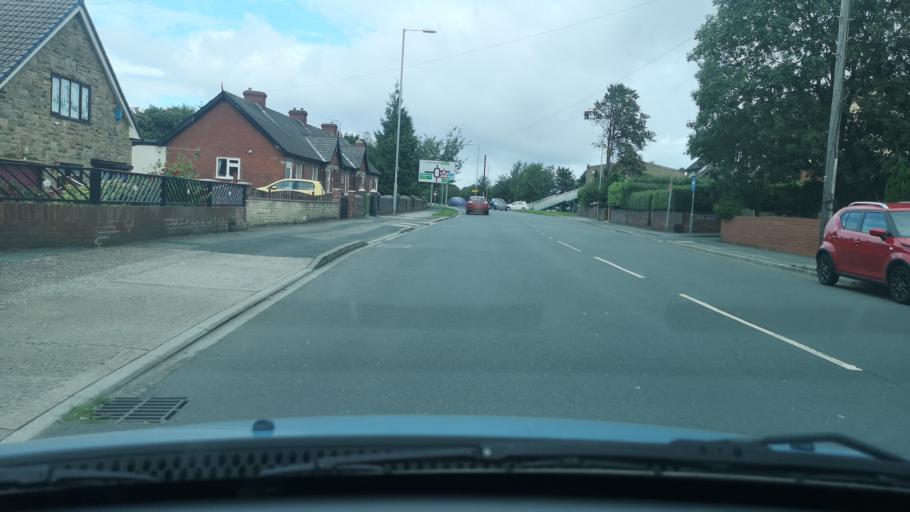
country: GB
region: England
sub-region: City and Borough of Wakefield
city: Ossett
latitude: 53.6919
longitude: -1.5899
